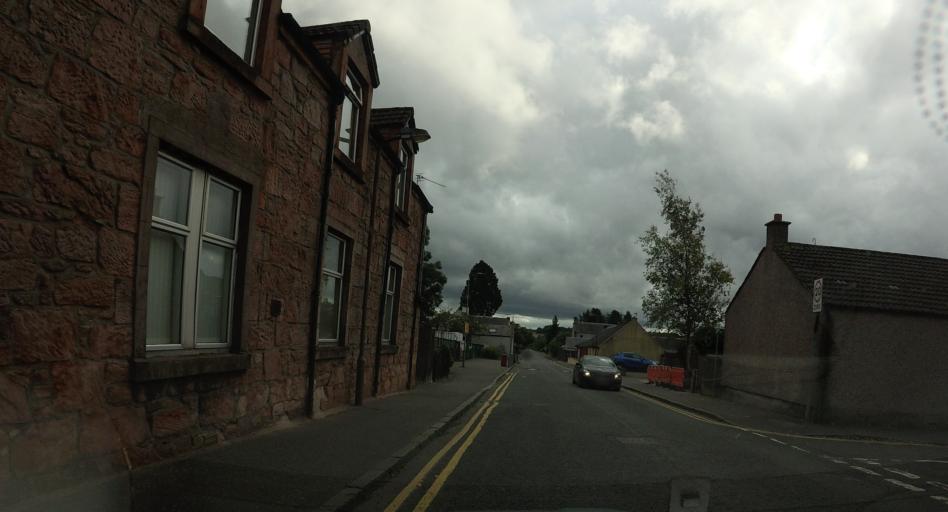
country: GB
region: Scotland
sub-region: Clackmannanshire
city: Alva
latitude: 56.1515
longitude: -3.7983
